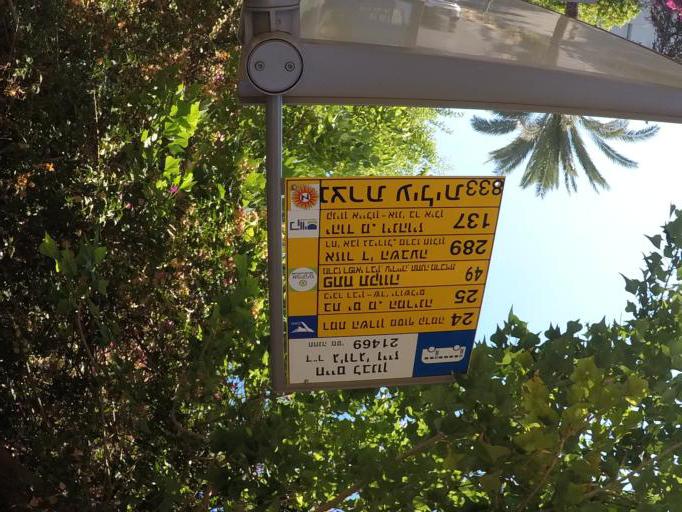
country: IL
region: Tel Aviv
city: Ramat Gan
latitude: 32.1111
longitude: 34.8017
